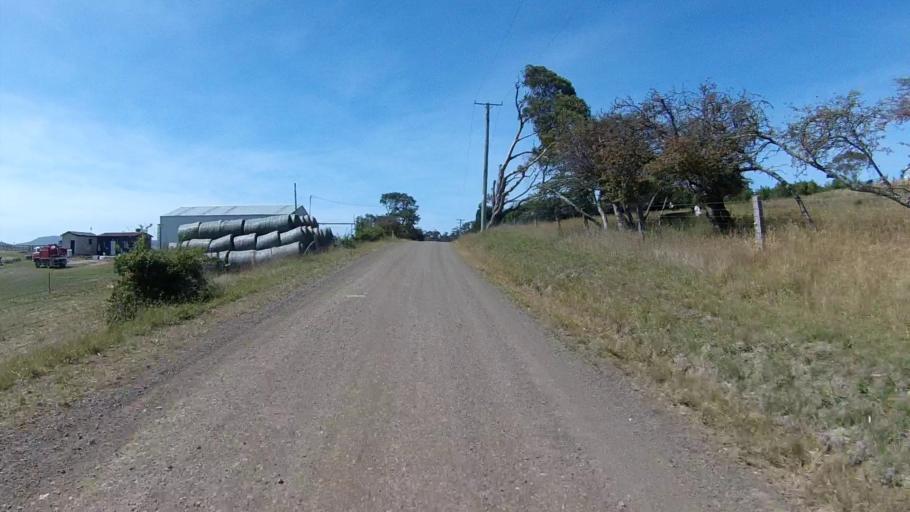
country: AU
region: Tasmania
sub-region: Sorell
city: Sorell
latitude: -42.7410
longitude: 147.5995
